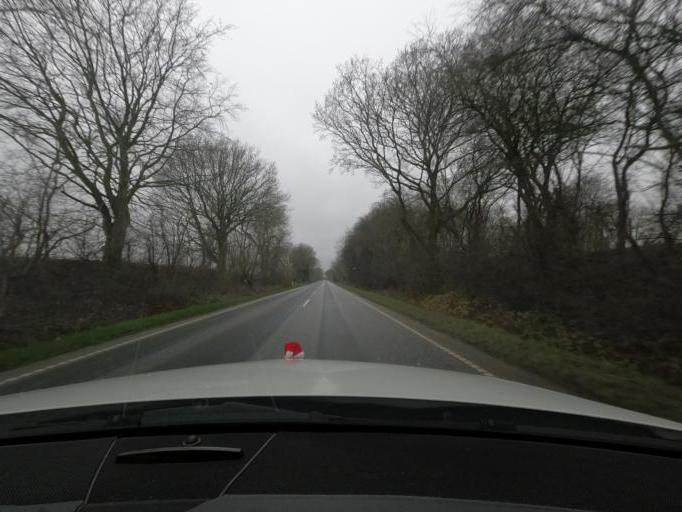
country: DK
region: South Denmark
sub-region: Haderslev Kommune
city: Starup
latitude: 55.2134
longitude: 9.5925
